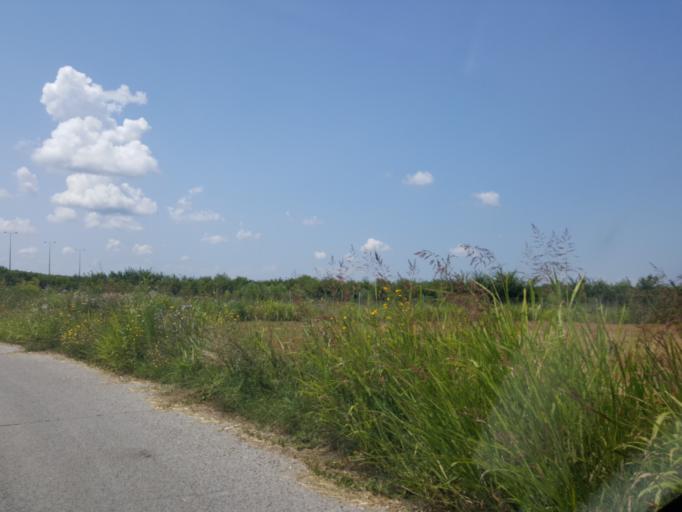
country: RS
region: Autonomna Pokrajina Vojvodina
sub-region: Sremski Okrug
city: Sid
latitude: 45.0480
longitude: 19.1755
